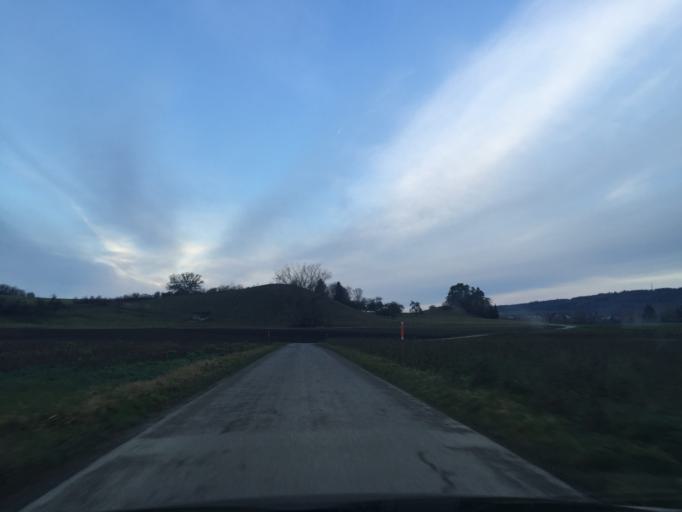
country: CH
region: Thurgau
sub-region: Frauenfeld District
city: Diessenhofen
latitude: 47.6715
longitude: 8.7428
